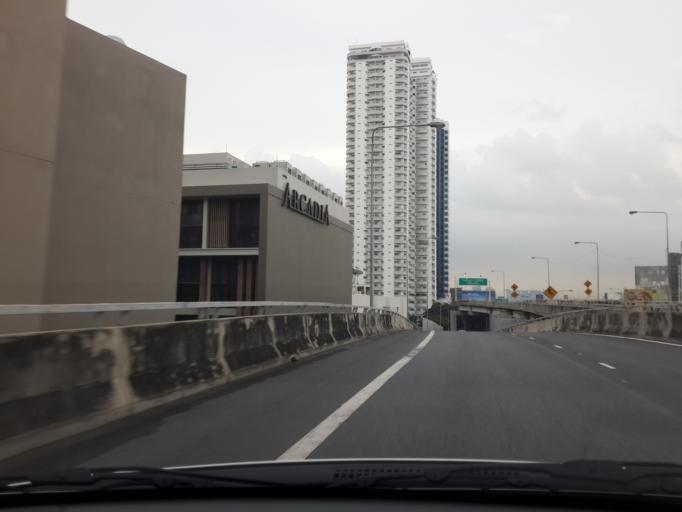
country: TH
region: Bangkok
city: Ratchathewi
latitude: 13.7463
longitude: 100.5499
